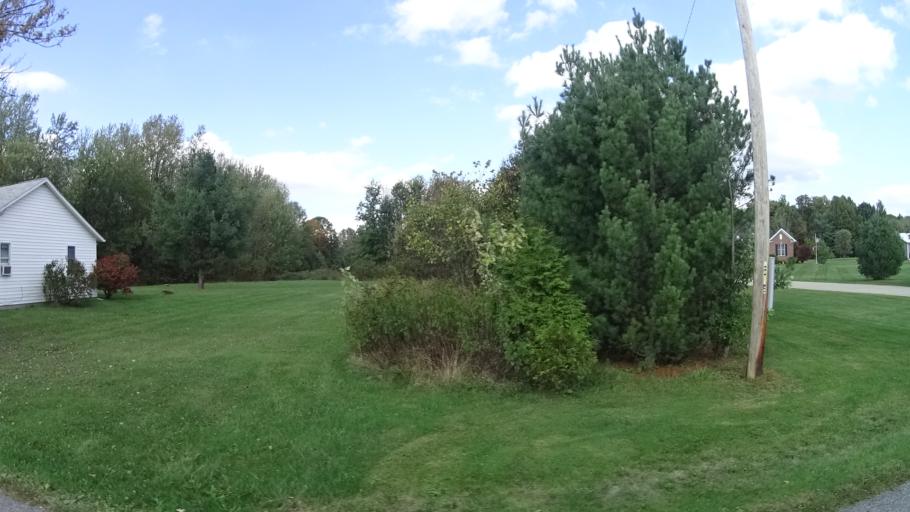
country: US
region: Ohio
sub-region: Lorain County
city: Grafton
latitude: 41.2524
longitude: -82.0810
